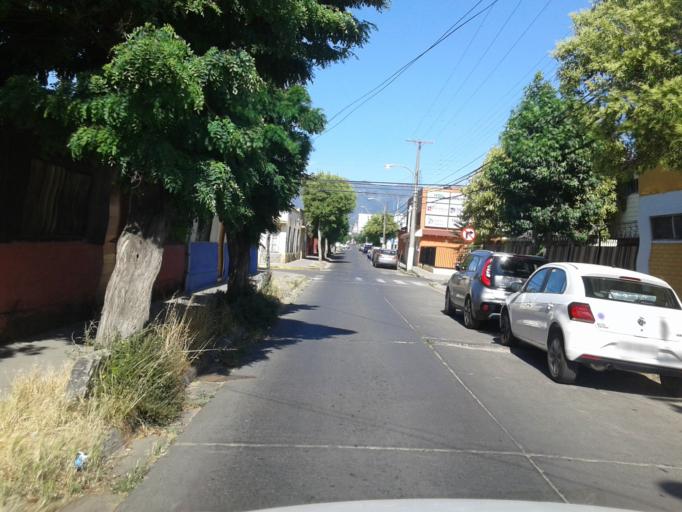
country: CL
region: Valparaiso
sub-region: Provincia de Quillota
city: Quillota
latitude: -32.8780
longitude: -71.2524
